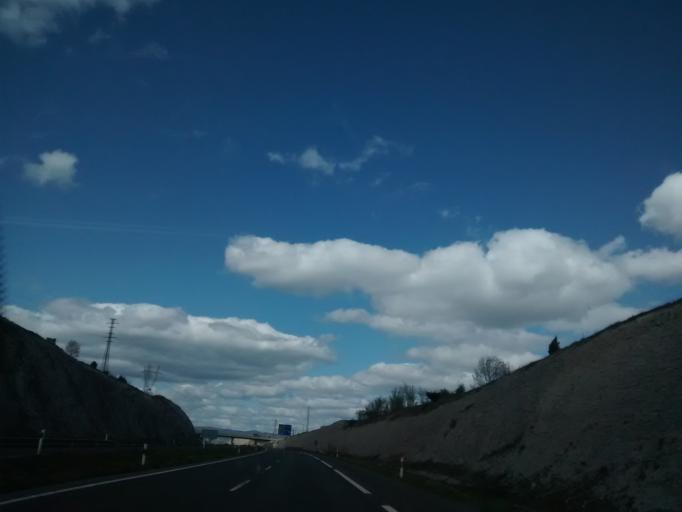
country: ES
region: Basque Country
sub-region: Provincia de Alava
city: Gasteiz / Vitoria
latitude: 42.8302
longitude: -2.7577
